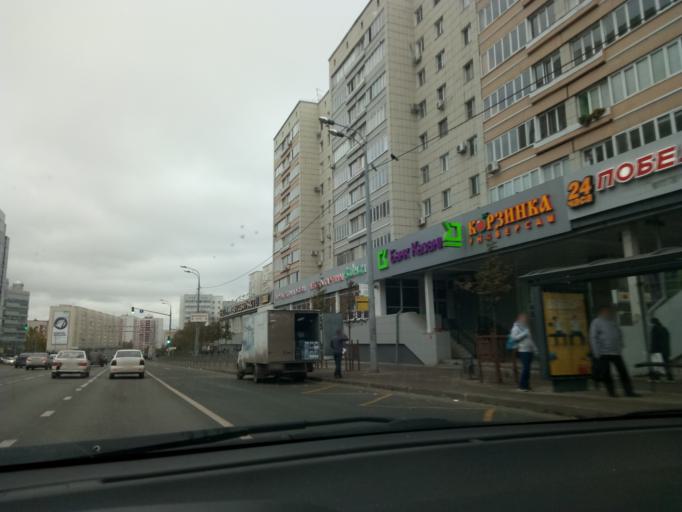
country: RU
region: Tatarstan
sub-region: Gorod Kazan'
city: Kazan
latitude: 55.7891
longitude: 49.1518
